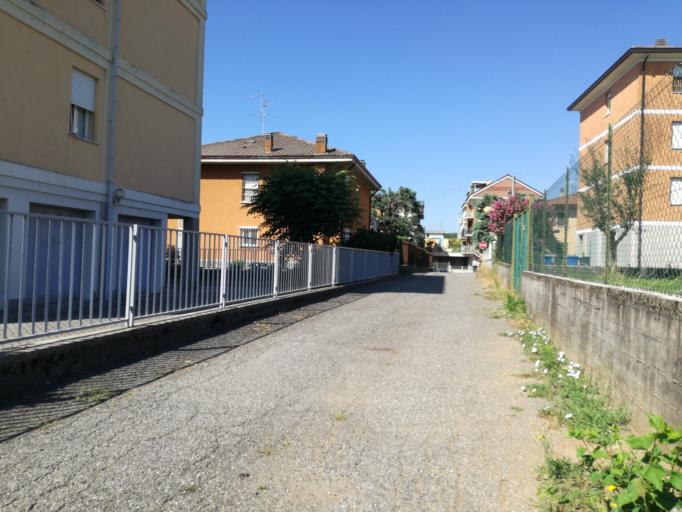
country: IT
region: Lombardy
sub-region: Provincia di Monza e Brianza
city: Porto d'Adda
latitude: 45.6649
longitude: 9.4782
